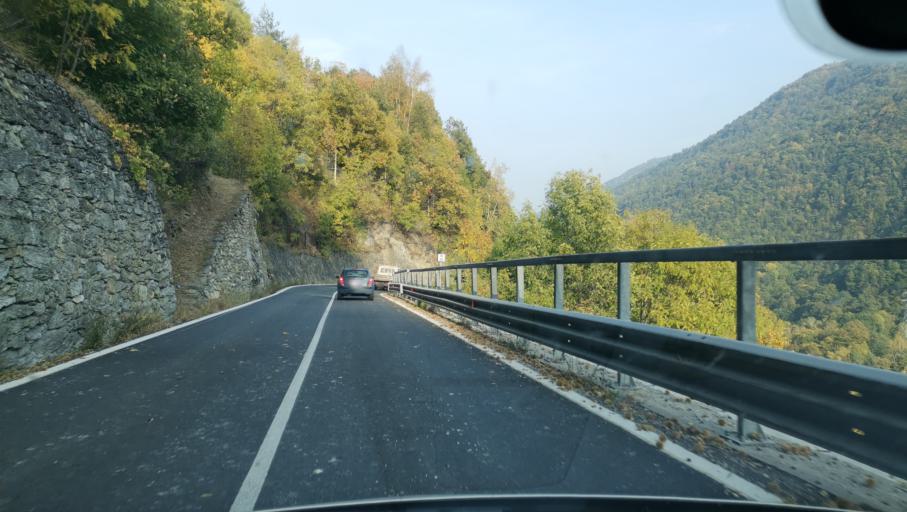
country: IT
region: Piedmont
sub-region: Provincia di Torino
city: Exilles
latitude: 45.1055
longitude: 6.9472
